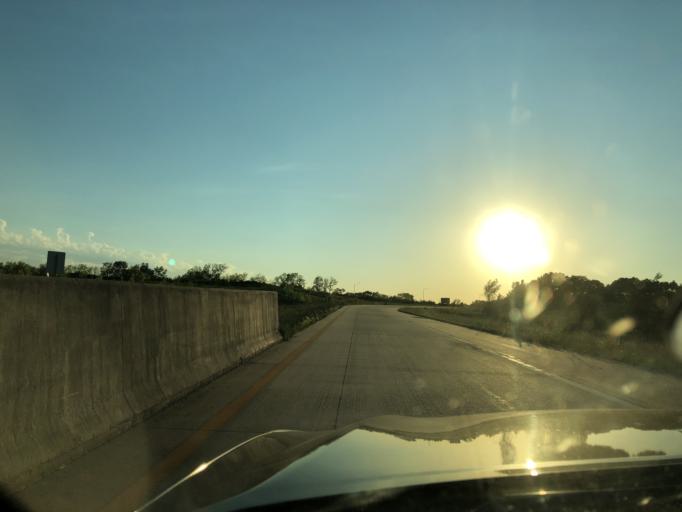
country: US
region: Kansas
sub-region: Leavenworth County
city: Basehor
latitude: 39.1184
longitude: -94.8948
